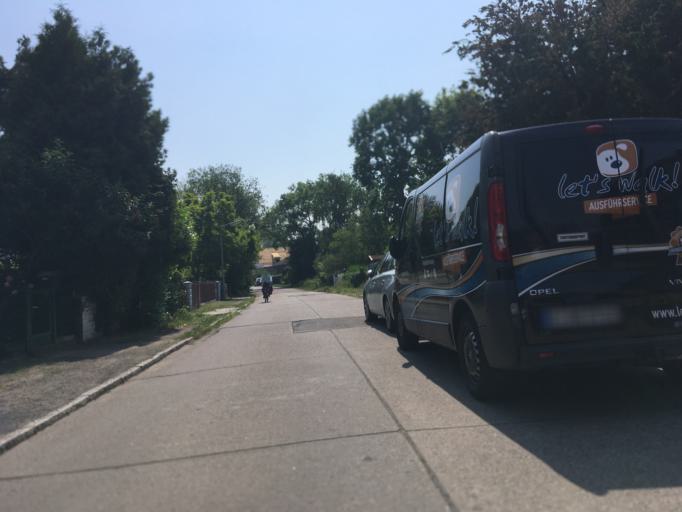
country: DE
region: Berlin
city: Heiligensee
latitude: 52.6155
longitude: 13.2234
